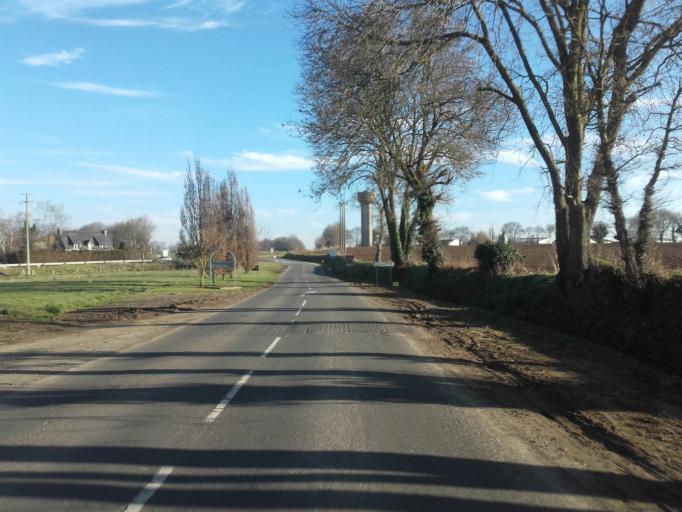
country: FR
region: Brittany
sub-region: Departement des Cotes-d'Armor
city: Goudelin
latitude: 48.6087
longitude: -3.0121
